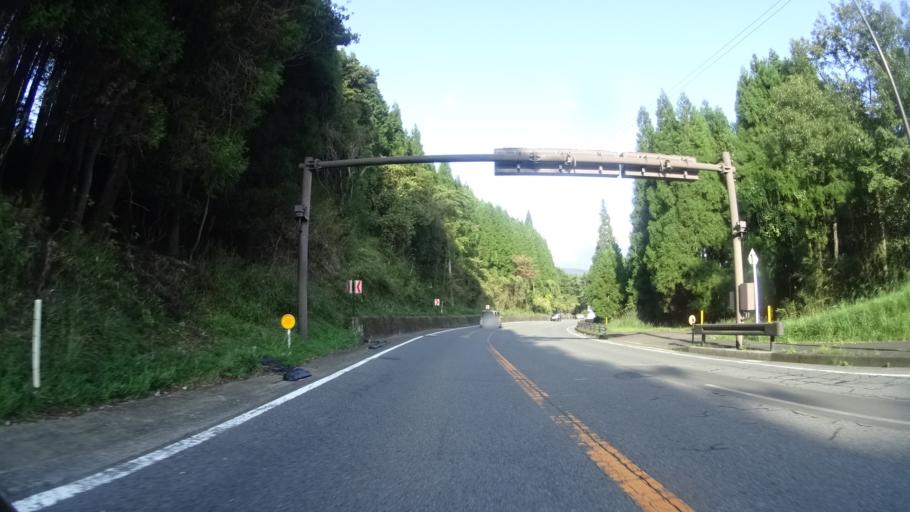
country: JP
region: Oita
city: Tsukawaki
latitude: 33.2580
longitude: 131.3187
